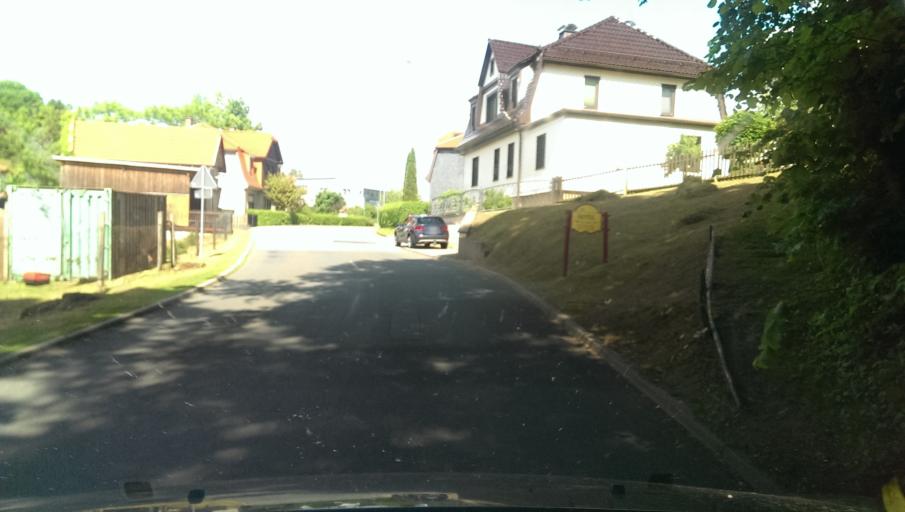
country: DE
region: Thuringia
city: Elgersburg
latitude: 50.7062
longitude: 10.8467
